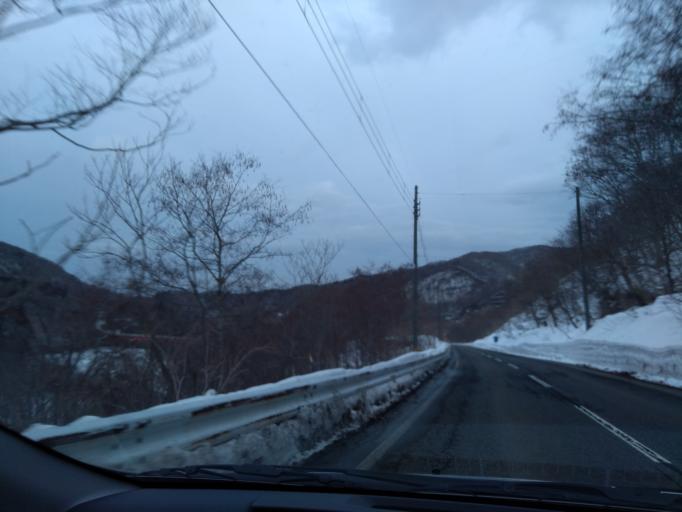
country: JP
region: Iwate
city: Kitakami
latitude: 39.2338
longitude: 140.9293
